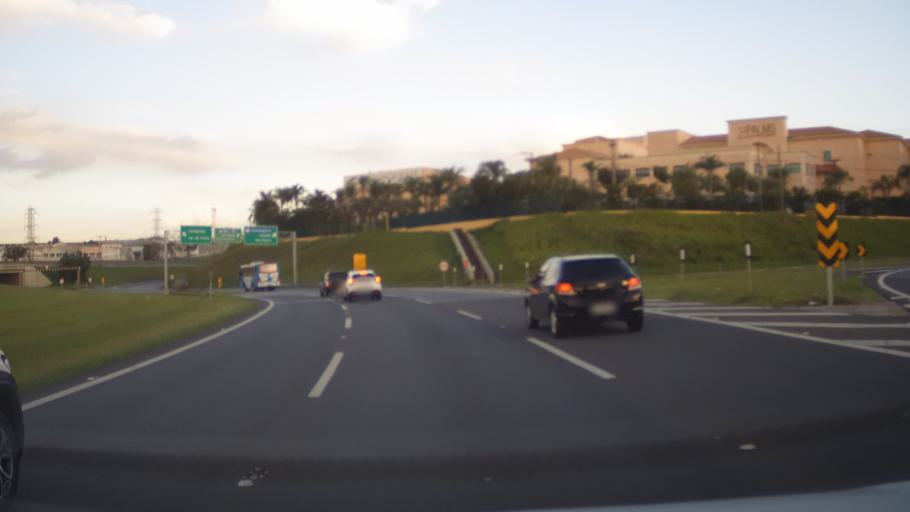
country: BR
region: Sao Paulo
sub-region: Campinas
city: Campinas
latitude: -22.9342
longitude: -47.0747
